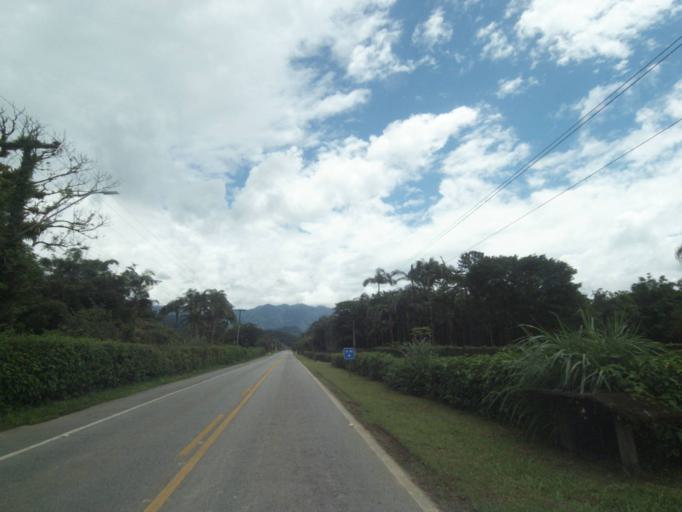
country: BR
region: Parana
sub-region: Antonina
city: Antonina
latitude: -25.4520
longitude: -48.8652
